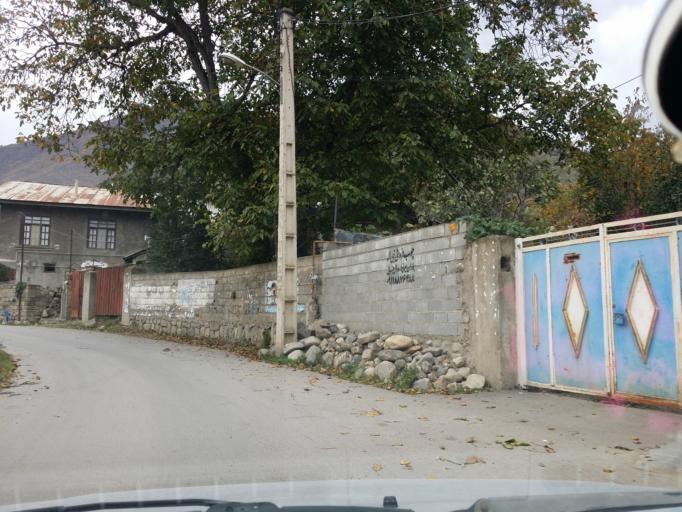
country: IR
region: Mazandaran
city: `Abbasabad
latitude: 36.5005
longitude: 51.1464
